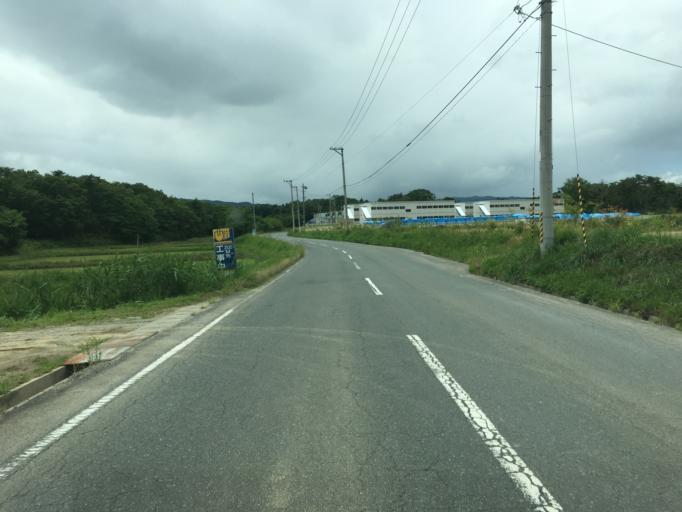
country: JP
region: Miyagi
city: Marumori
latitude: 37.7429
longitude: 140.9399
